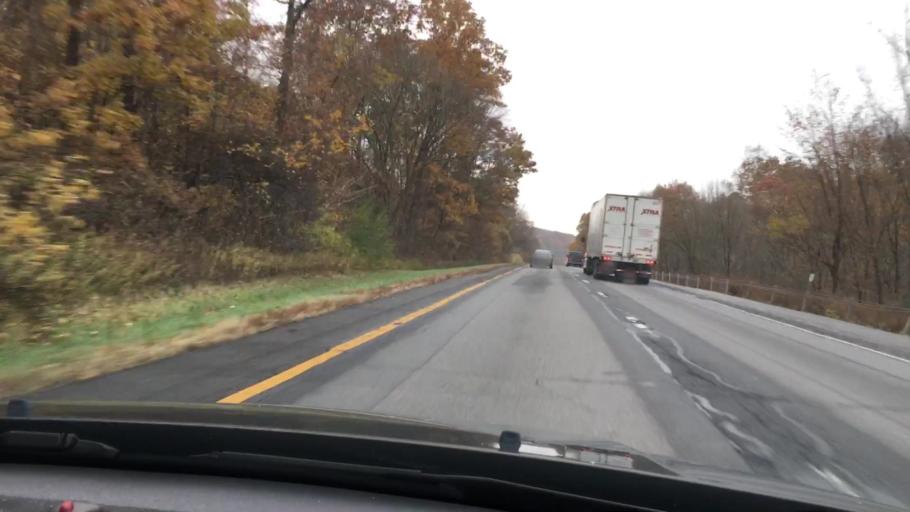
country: US
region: New York
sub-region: Putnam County
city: Lake Carmel
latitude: 41.4856
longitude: -73.6576
